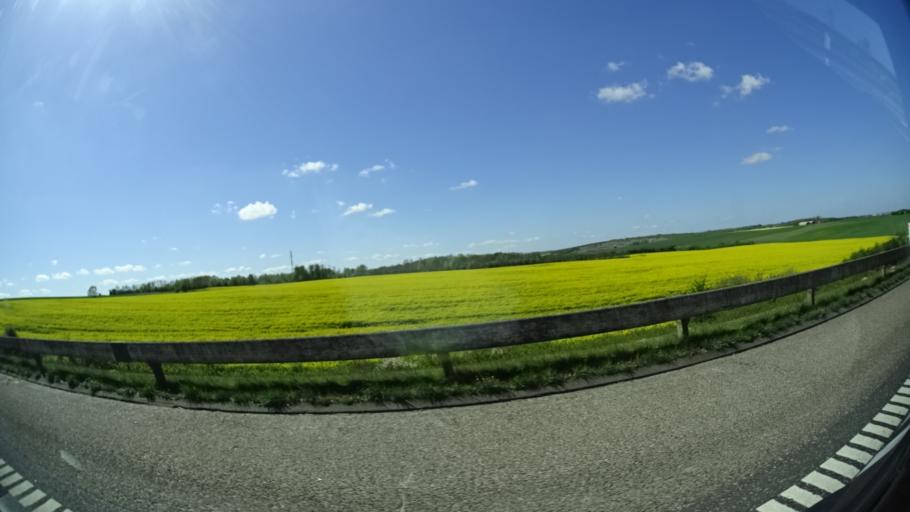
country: DK
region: Central Jutland
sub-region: Randers Kommune
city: Assentoft
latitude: 56.3750
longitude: 10.1175
